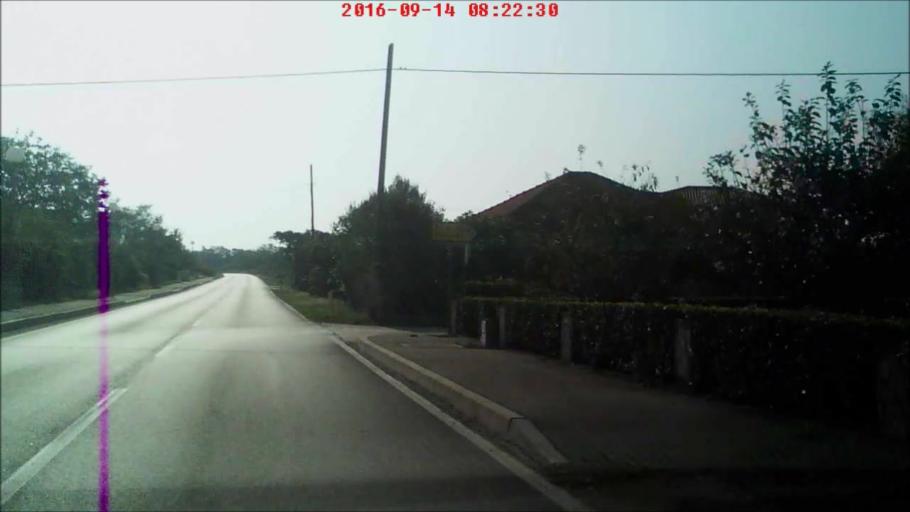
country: HR
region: Zadarska
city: Nin
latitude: 44.2174
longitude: 15.2196
